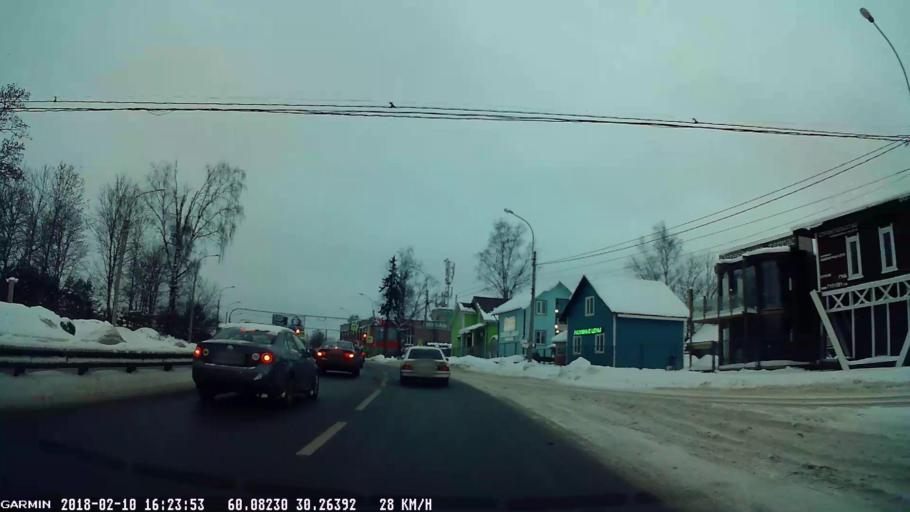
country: RU
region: St.-Petersburg
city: Pargolovo
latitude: 60.0827
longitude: 30.2636
